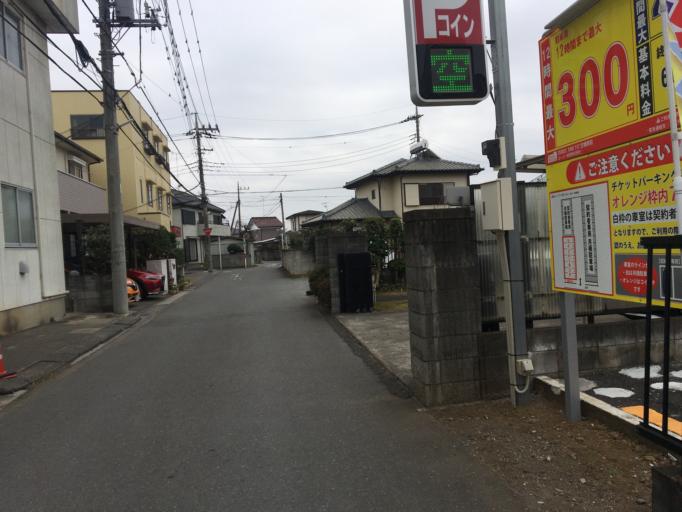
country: JP
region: Saitama
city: Sakado
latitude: 35.9080
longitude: 139.4065
